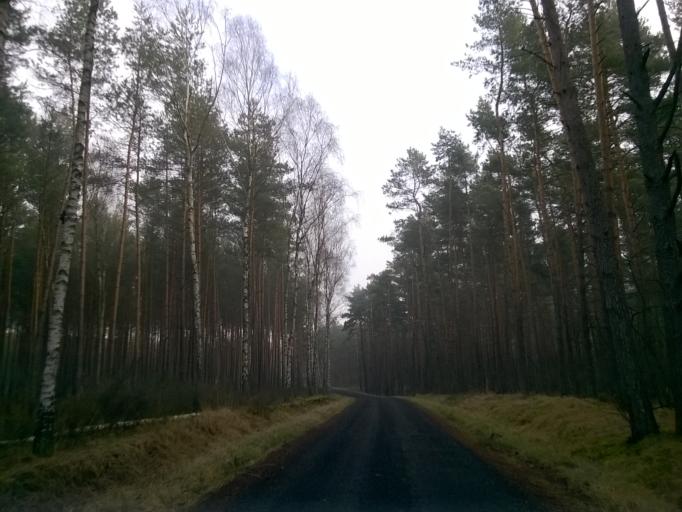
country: PL
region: Kujawsko-Pomorskie
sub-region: Powiat nakielski
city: Kcynia
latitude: 53.0450
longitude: 17.5398
